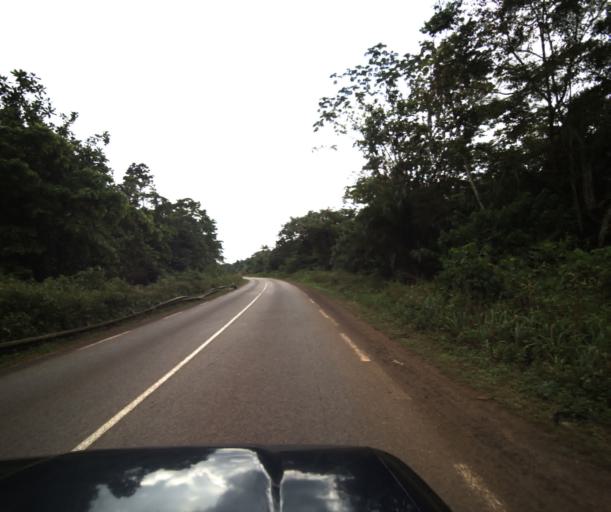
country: CM
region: Littoral
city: Edea
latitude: 3.8264
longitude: 10.3886
